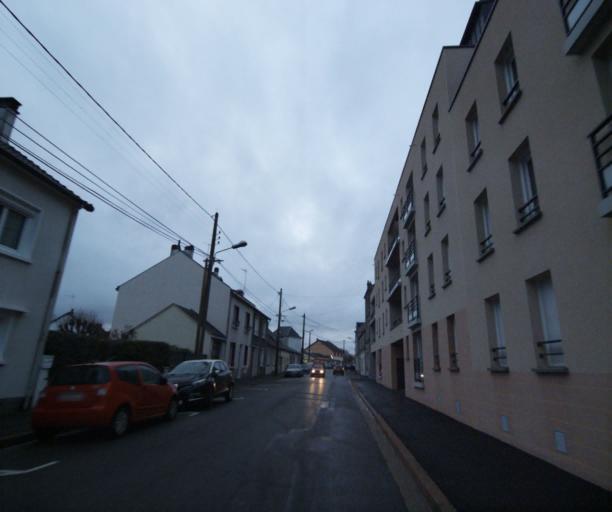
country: FR
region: Pays de la Loire
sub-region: Departement de la Sarthe
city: Coulaines
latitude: 48.0178
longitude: 0.1939
